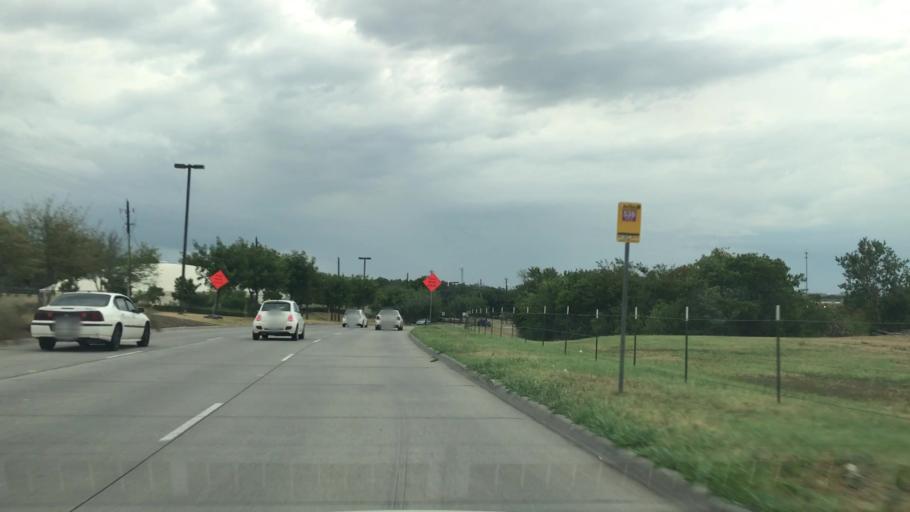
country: US
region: Texas
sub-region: Dallas County
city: Carrollton
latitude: 32.9753
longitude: -96.9101
